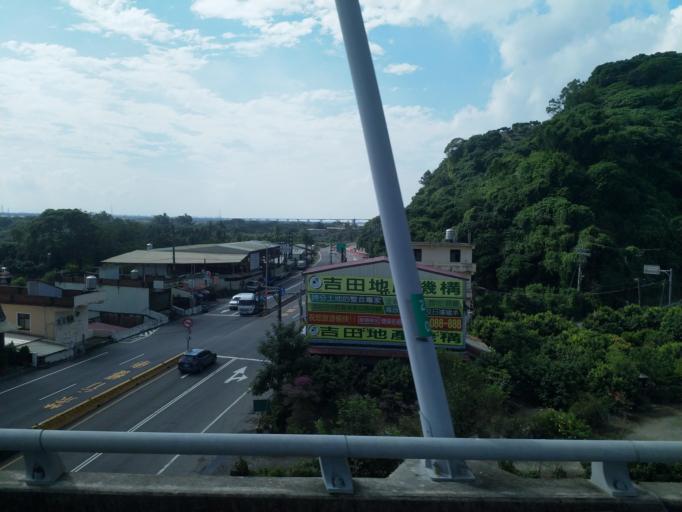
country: TW
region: Taiwan
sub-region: Pingtung
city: Pingtung
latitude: 22.7974
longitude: 120.4580
